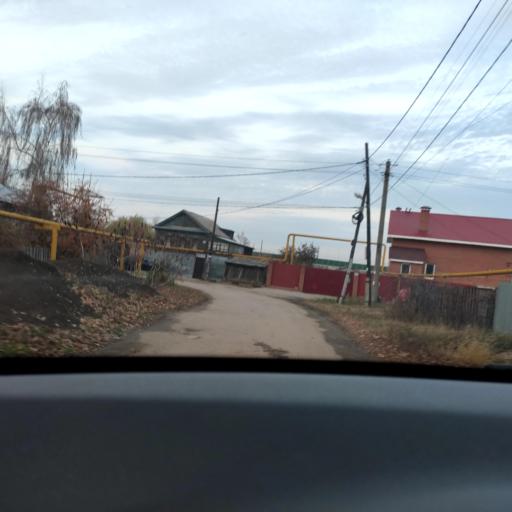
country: RU
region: Samara
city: Samara
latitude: 53.1620
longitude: 50.0825
